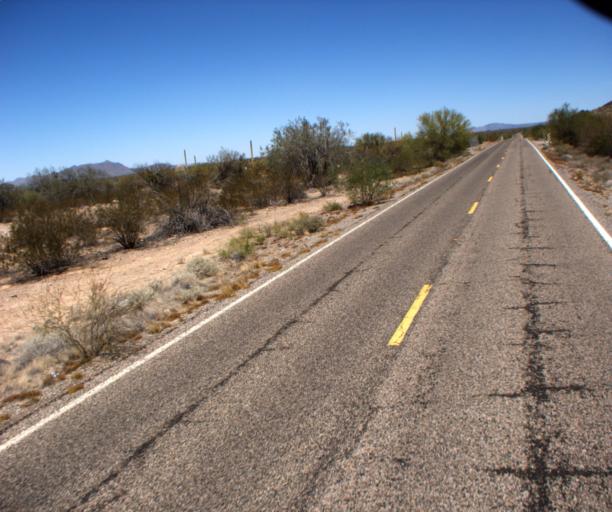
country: US
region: Arizona
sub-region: Pima County
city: Ajo
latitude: 32.2075
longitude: -112.7585
